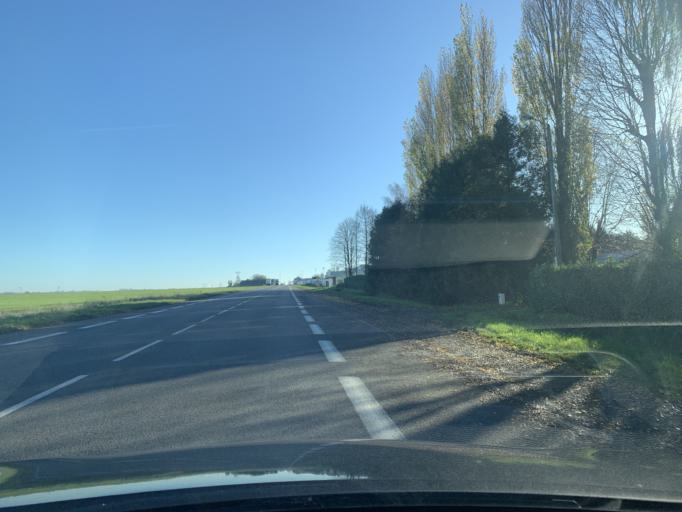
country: FR
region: Nord-Pas-de-Calais
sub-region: Departement du Nord
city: Escaudoeuvres
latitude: 50.1647
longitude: 3.2780
